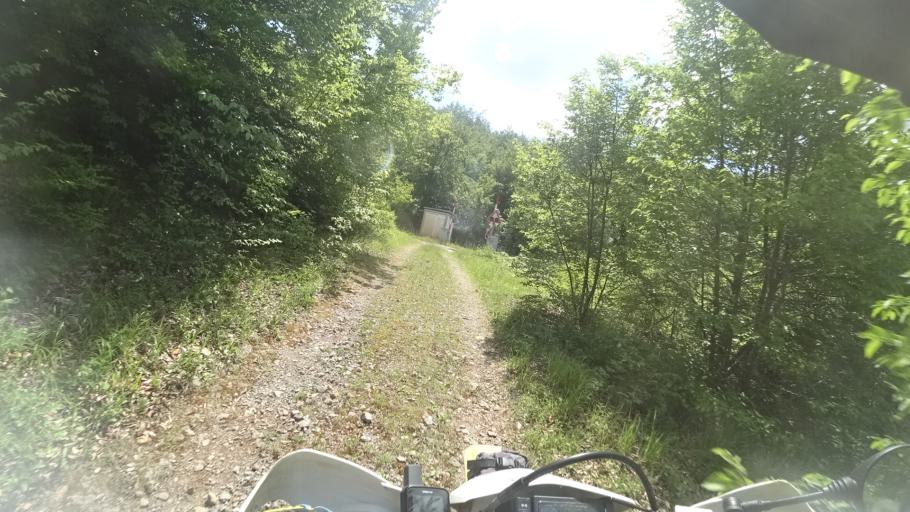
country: HR
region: Zadarska
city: Gracac
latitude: 44.2593
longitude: 15.9350
